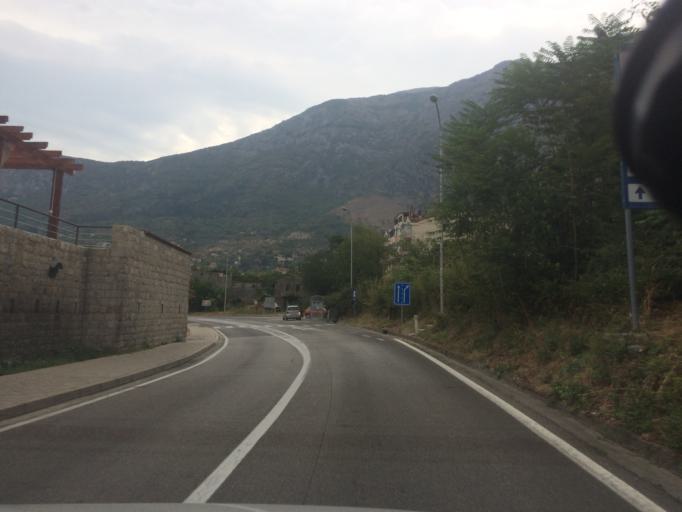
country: ME
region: Kotor
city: Risan
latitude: 42.5071
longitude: 18.6952
